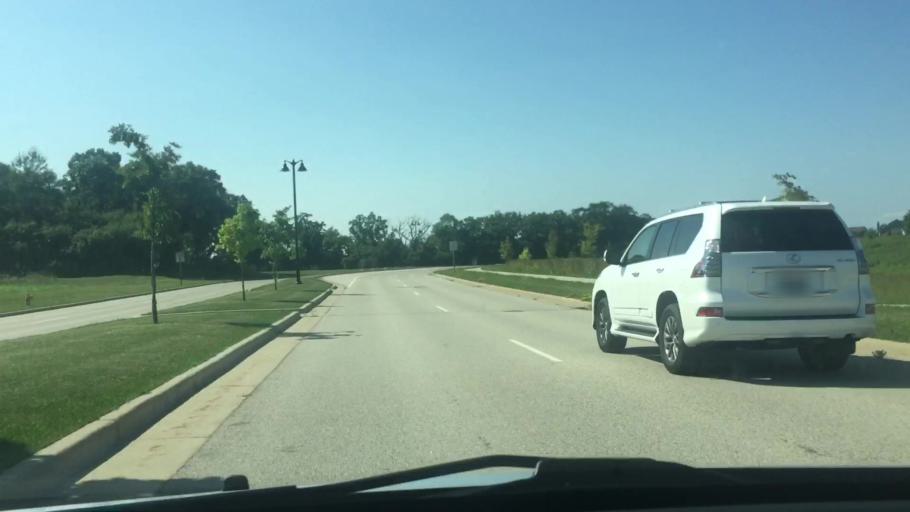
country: US
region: Wisconsin
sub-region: Waukesha County
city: Delafield
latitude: 43.0688
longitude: -88.4561
